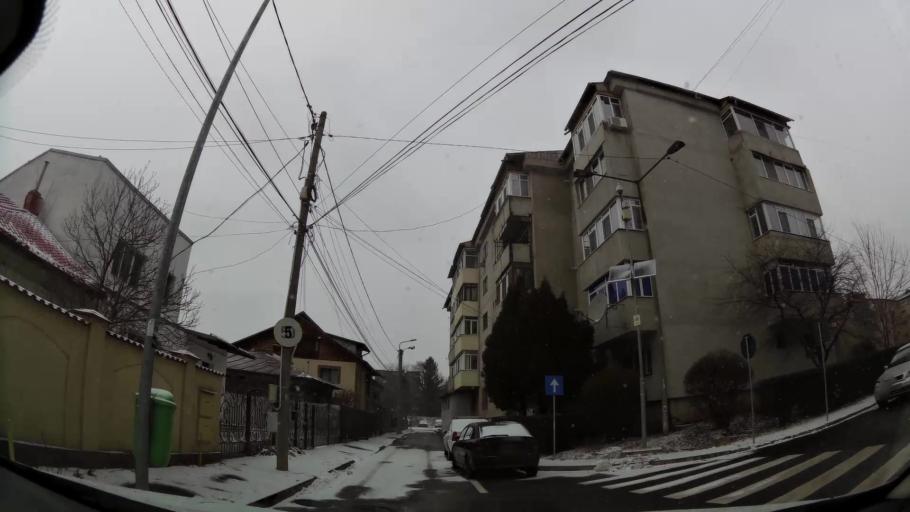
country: RO
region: Dambovita
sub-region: Municipiul Targoviste
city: Targoviste
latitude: 44.9174
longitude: 25.4624
